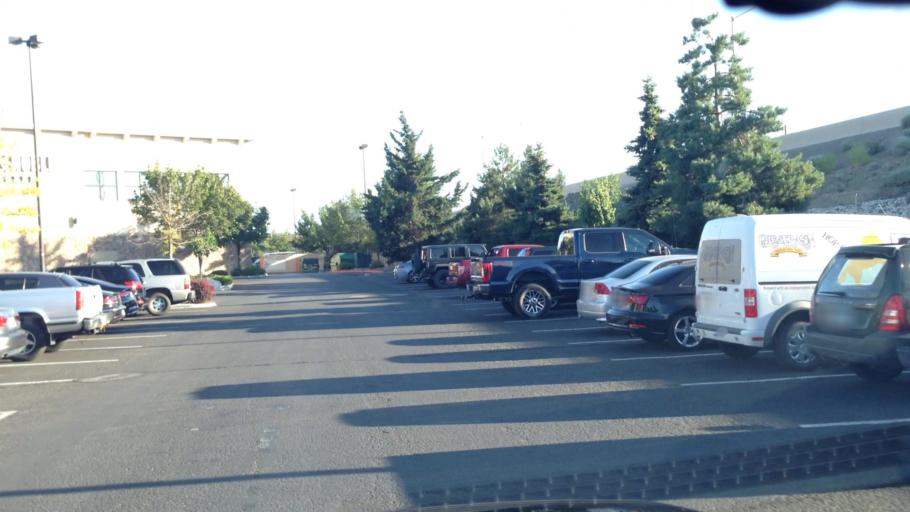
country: US
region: Nevada
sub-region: Washoe County
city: Reno
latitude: 39.4763
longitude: -119.7903
